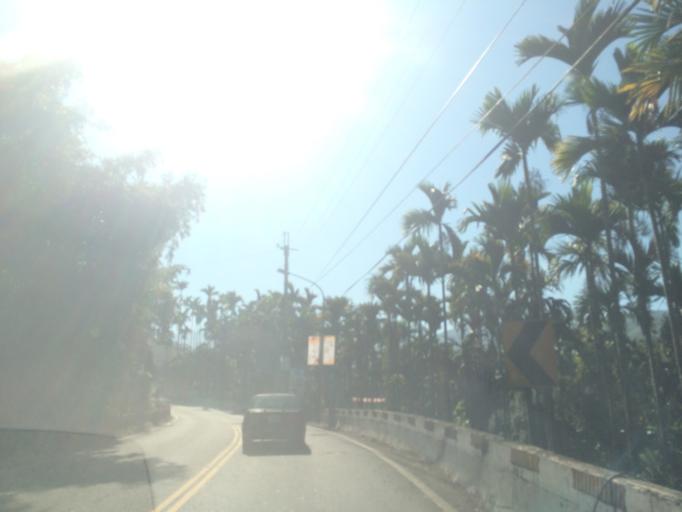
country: TW
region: Taiwan
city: Lugu
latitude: 23.7212
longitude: 120.7781
